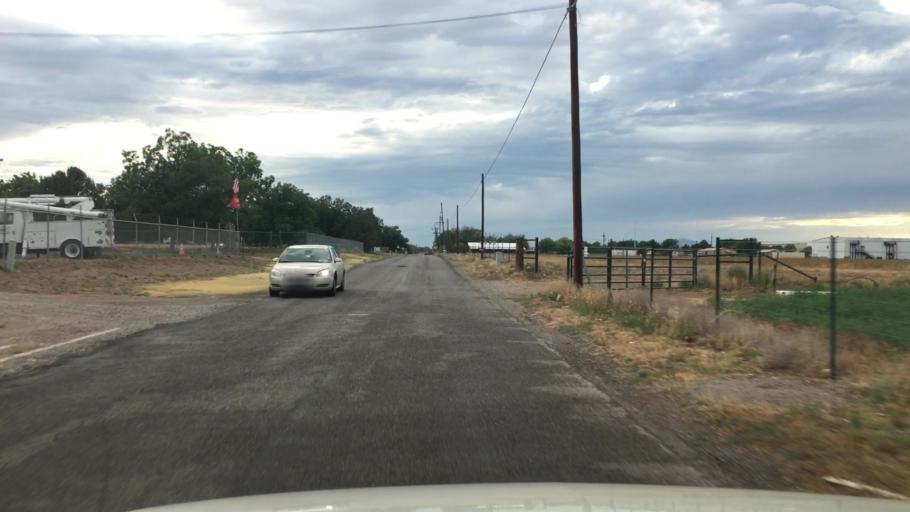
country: US
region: New Mexico
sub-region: Chaves County
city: Roswell
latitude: 33.4160
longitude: -104.5012
